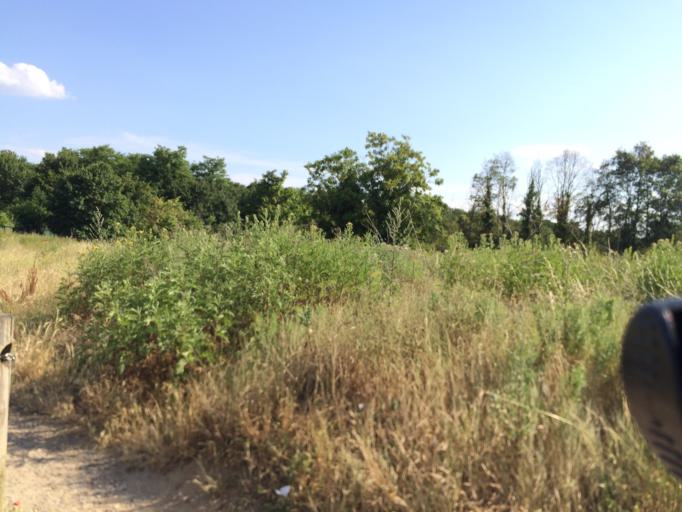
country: FR
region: Ile-de-France
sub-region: Departement de l'Essonne
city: Montgeron
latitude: 48.6887
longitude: 2.4387
